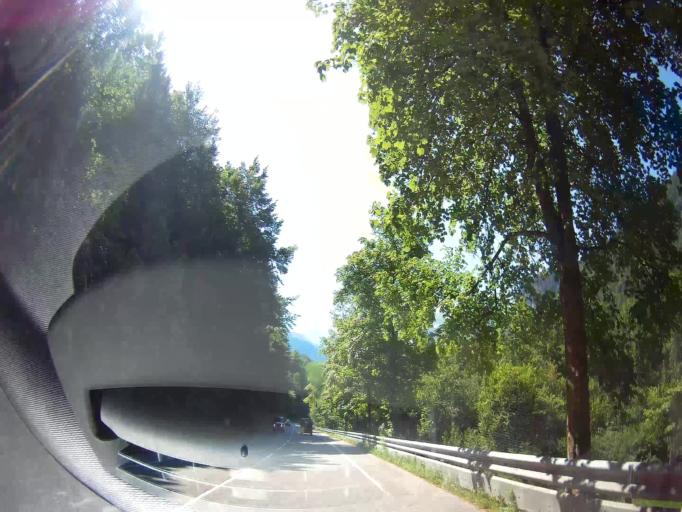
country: DE
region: Bavaria
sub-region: Upper Bavaria
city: Marktschellenberg
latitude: 47.6640
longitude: 13.0354
